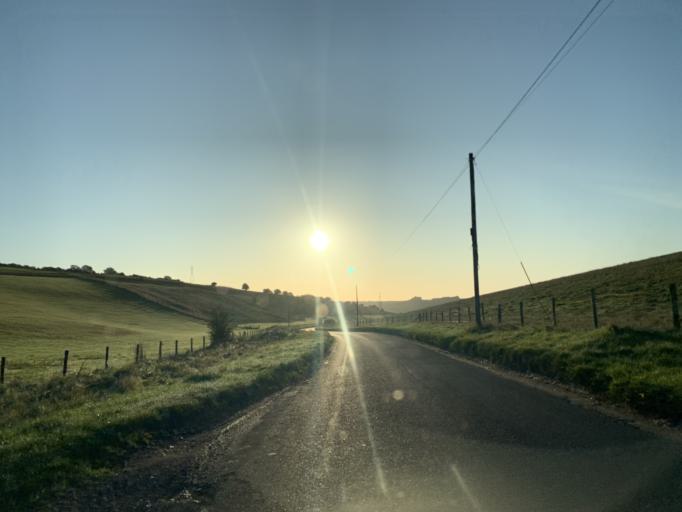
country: GB
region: England
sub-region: Wiltshire
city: Woodford
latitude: 51.1272
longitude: -1.8475
